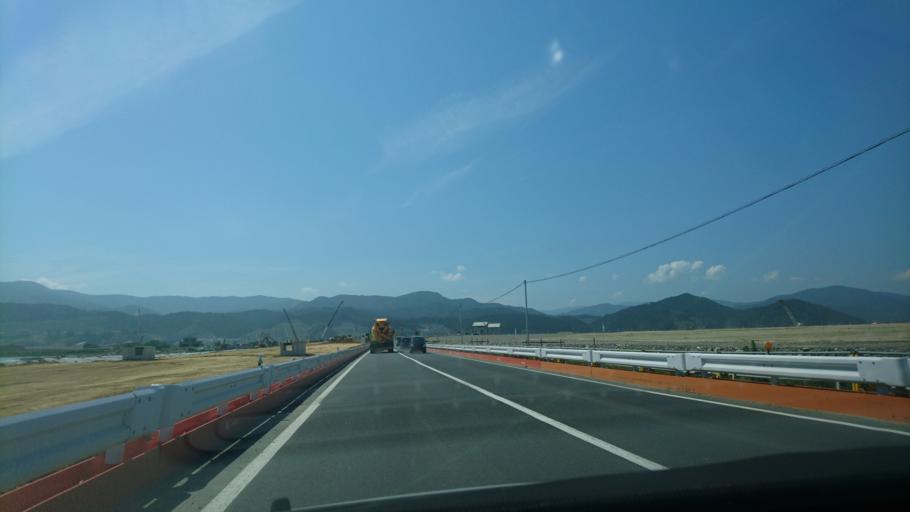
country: JP
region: Iwate
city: Ofunato
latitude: 39.0096
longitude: 141.6351
